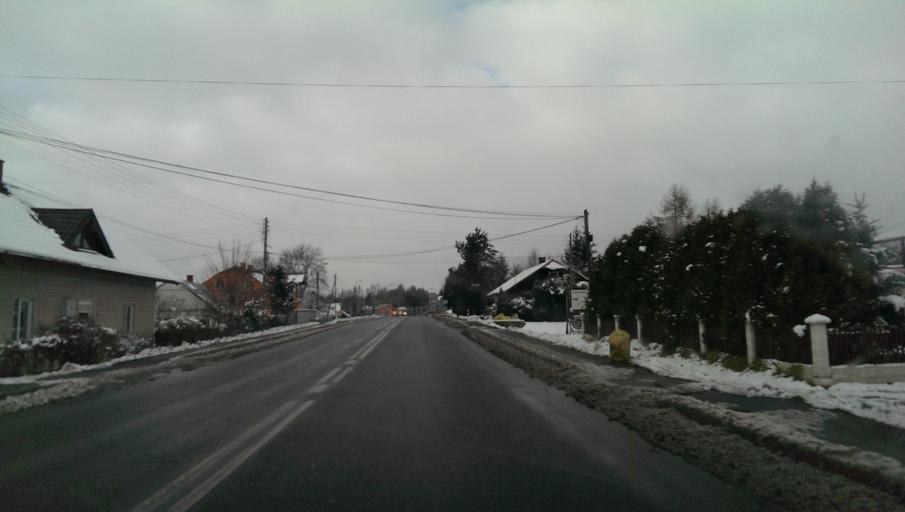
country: PL
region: Subcarpathian Voivodeship
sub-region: Powiat brzozowski
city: Humniska
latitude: 49.6834
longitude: 22.0410
